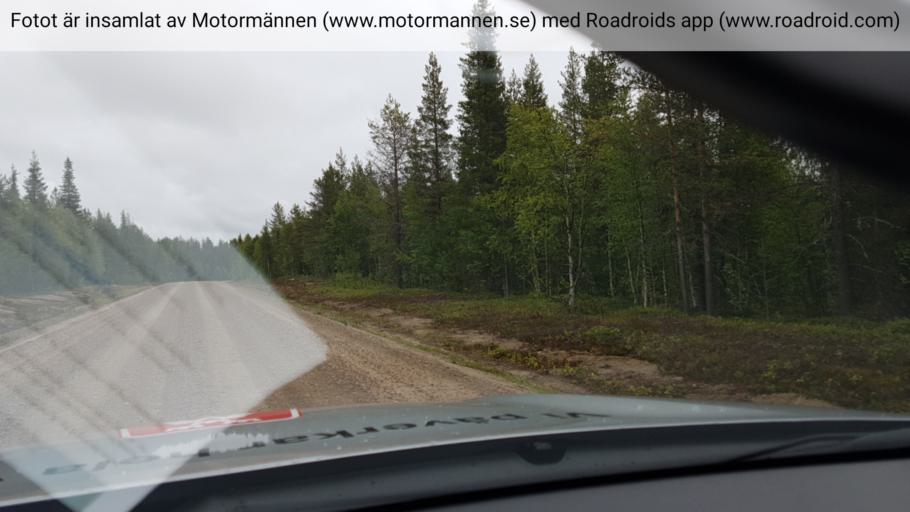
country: SE
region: Norrbotten
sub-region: Gallivare Kommun
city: Gaellivare
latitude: 66.7419
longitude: 20.8959
